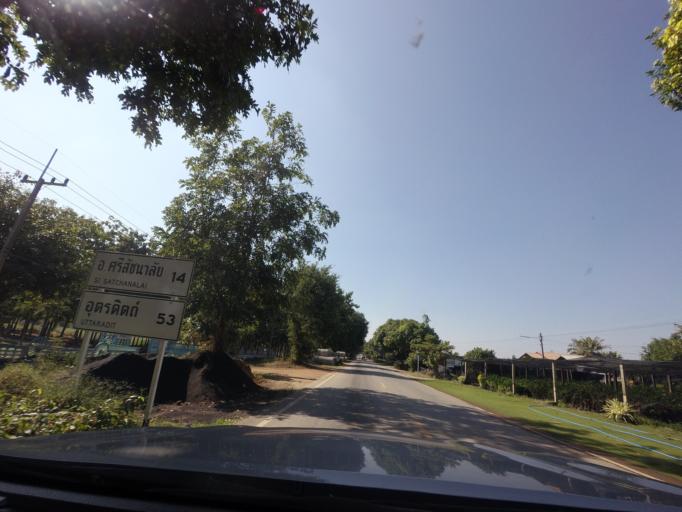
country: TH
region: Sukhothai
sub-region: Amphoe Si Satchanalai
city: Si Satchanalai
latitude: 17.4177
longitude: 99.7975
